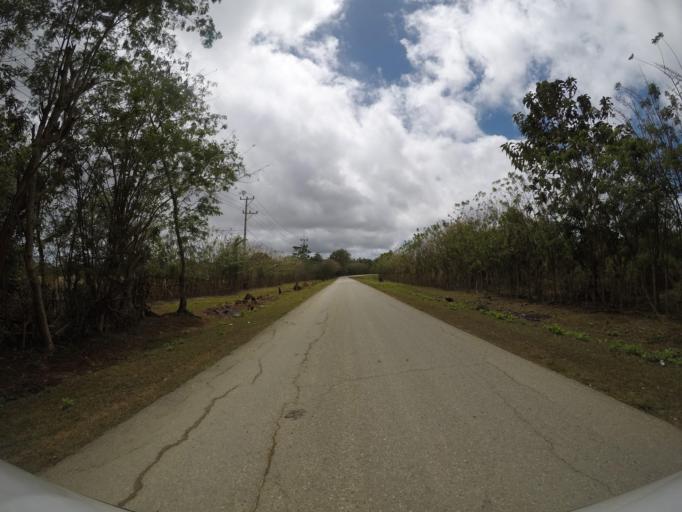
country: TL
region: Lautem
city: Lospalos
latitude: -8.4591
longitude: 126.9991
